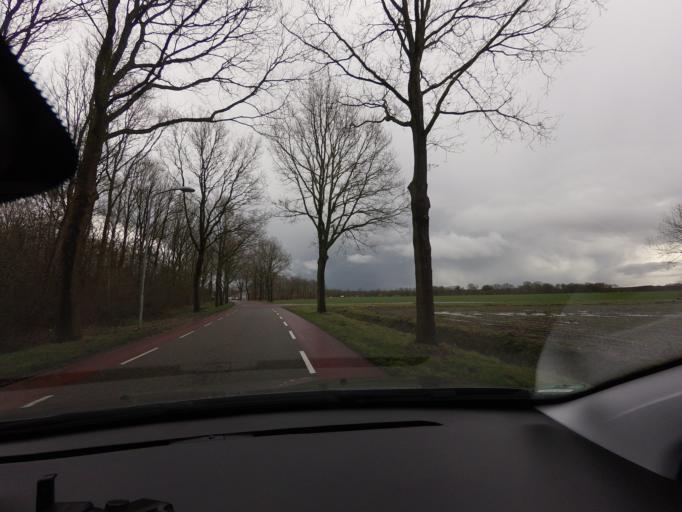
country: NL
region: Drenthe
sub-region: Gemeente Borger-Odoorn
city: Borger
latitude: 52.9799
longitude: 6.7874
